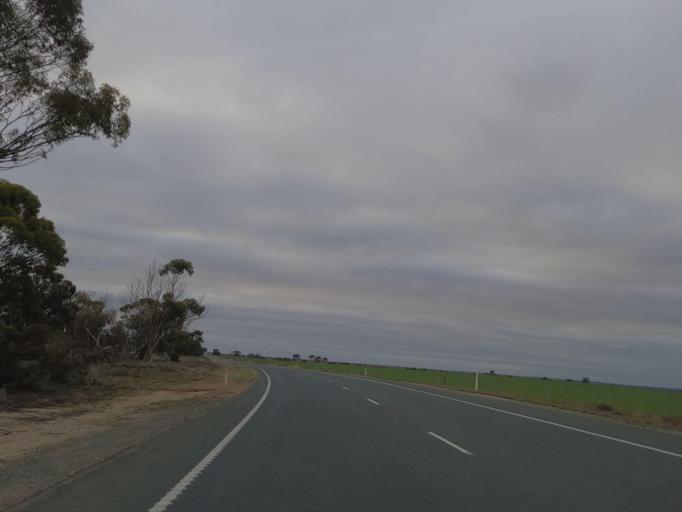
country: AU
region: Victoria
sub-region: Swan Hill
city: Swan Hill
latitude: -35.5627
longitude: 143.7826
